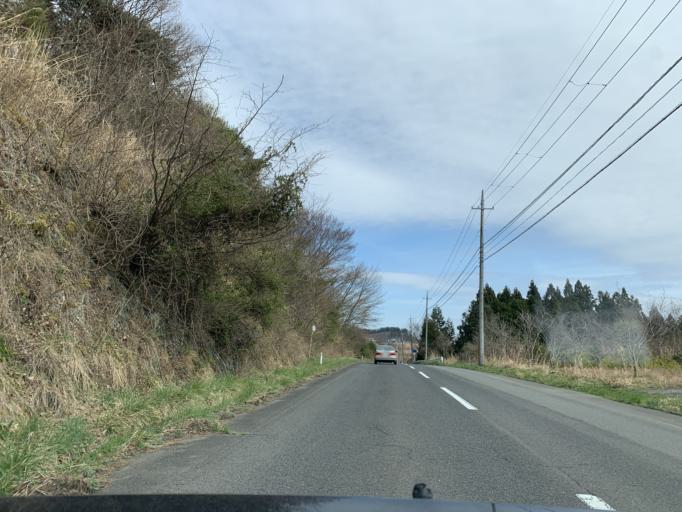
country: JP
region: Iwate
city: Ichinoseki
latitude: 38.8260
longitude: 141.2917
